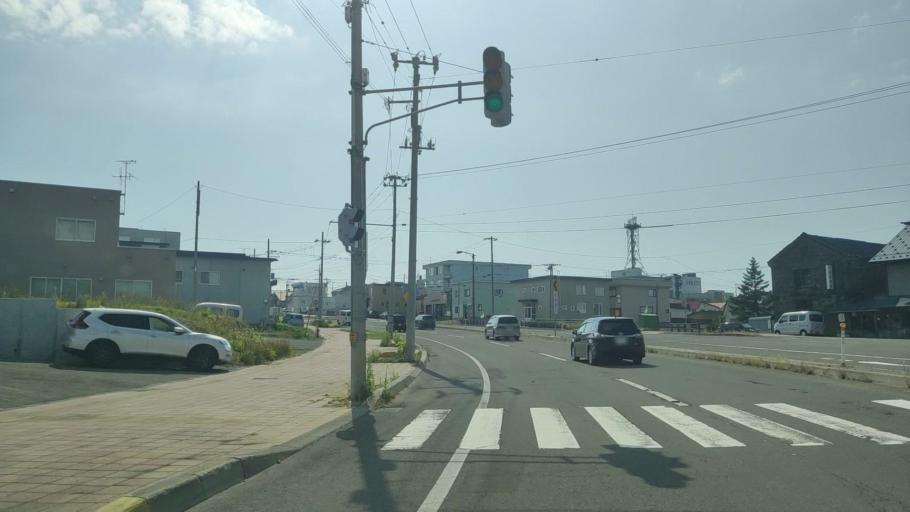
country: JP
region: Hokkaido
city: Rumoi
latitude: 43.9425
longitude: 141.6423
